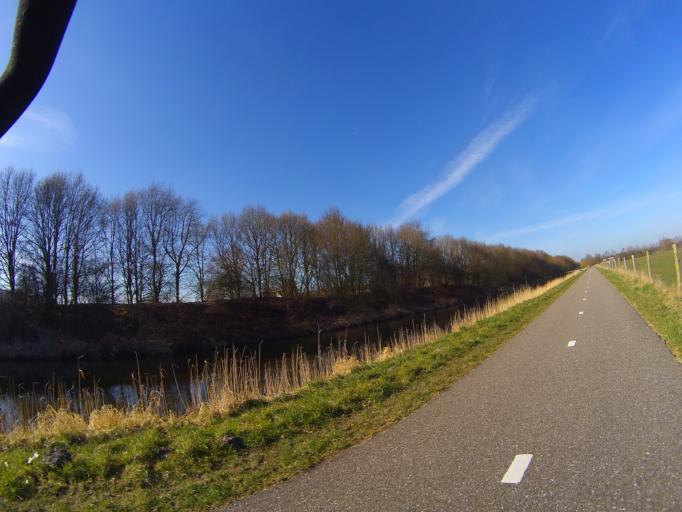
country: NL
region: Utrecht
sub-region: Gemeente Leusden
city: Leusden
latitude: 52.1245
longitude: 5.4462
